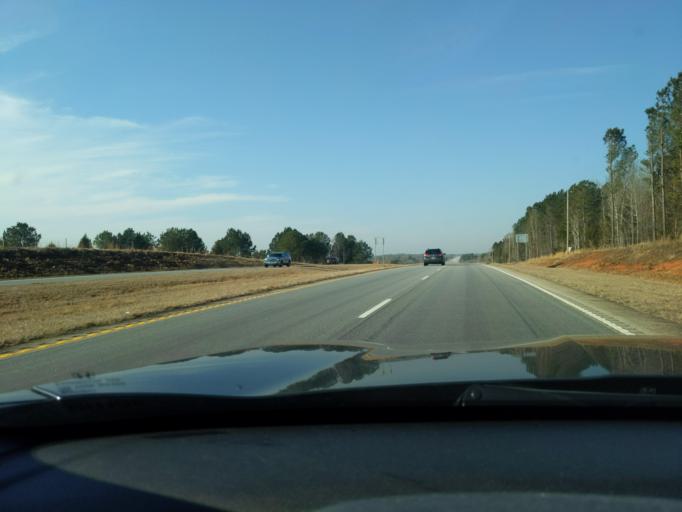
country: US
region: South Carolina
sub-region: Abbeville County
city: Calhoun Falls
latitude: 34.1082
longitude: -82.5225
